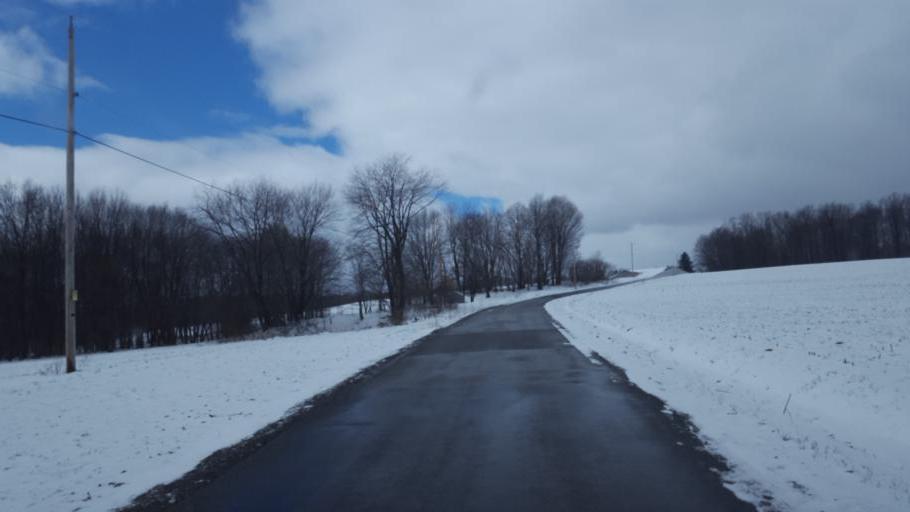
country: US
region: Pennsylvania
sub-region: Mercer County
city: Stoneboro
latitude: 41.4069
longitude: -80.0951
